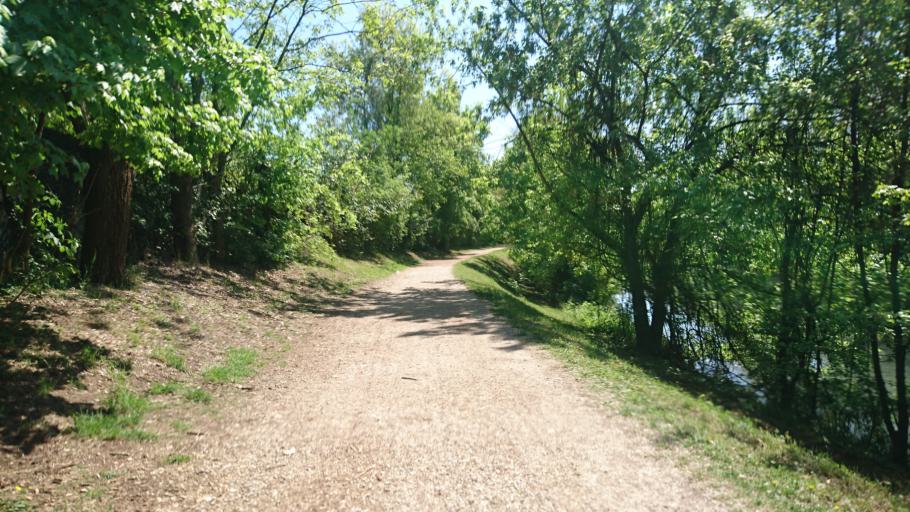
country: IT
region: Veneto
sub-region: Provincia di Treviso
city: Casier
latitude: 45.6463
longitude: 12.2744
